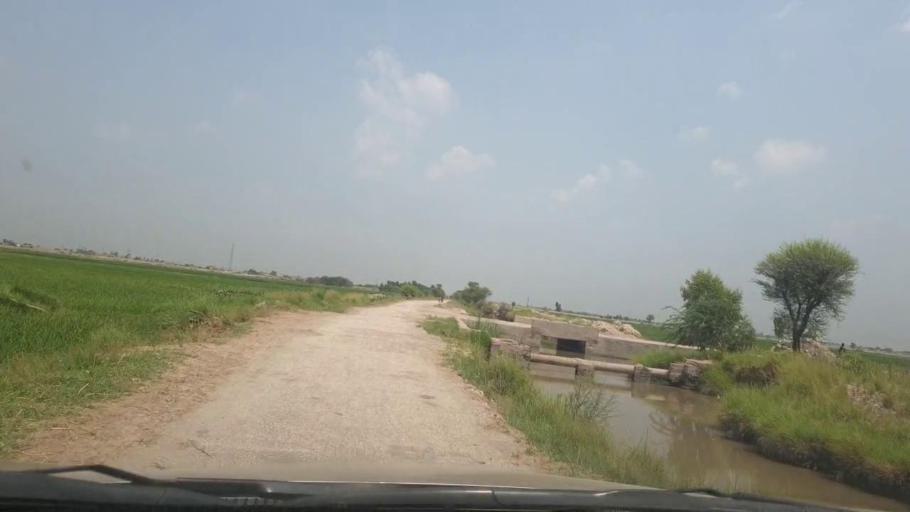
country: PK
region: Sindh
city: Ratodero
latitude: 27.6918
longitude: 68.2331
